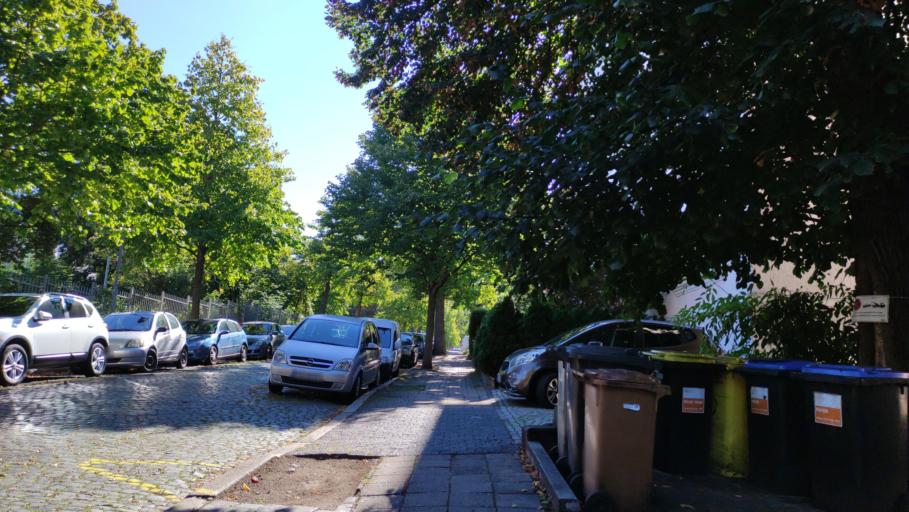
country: DE
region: Thuringia
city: Erfurt
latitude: 50.9680
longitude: 11.0335
